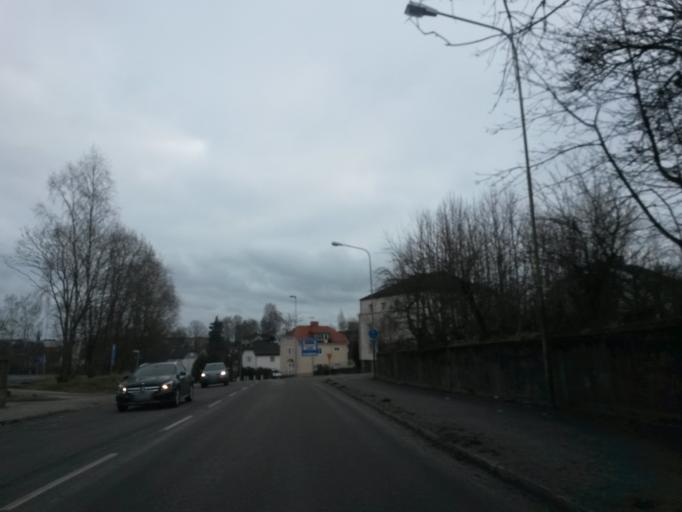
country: SE
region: Vaestra Goetaland
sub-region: Boras Kommun
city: Boras
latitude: 57.7264
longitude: 12.9190
